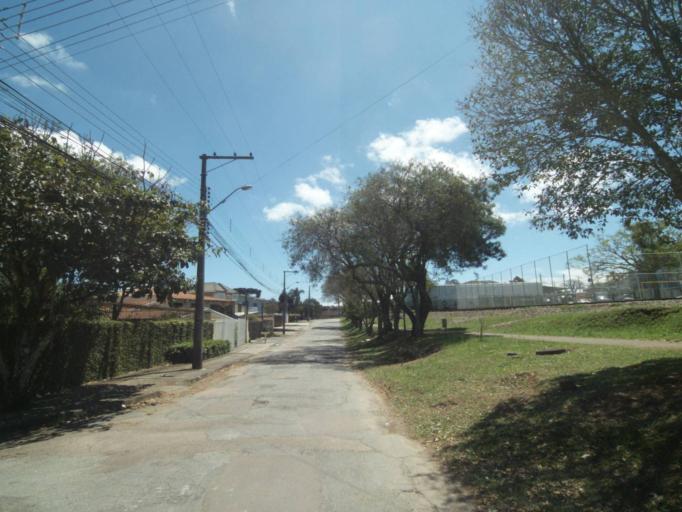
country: BR
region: Parana
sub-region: Curitiba
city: Curitiba
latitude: -25.3838
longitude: -49.2621
